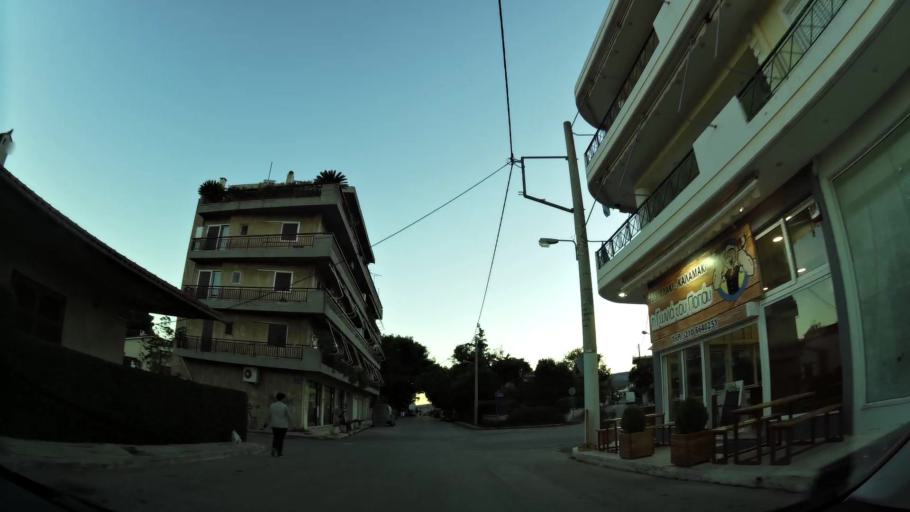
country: GR
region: Attica
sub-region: Nomarchia Anatolikis Attikis
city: Paiania
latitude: 37.9593
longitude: 23.8542
